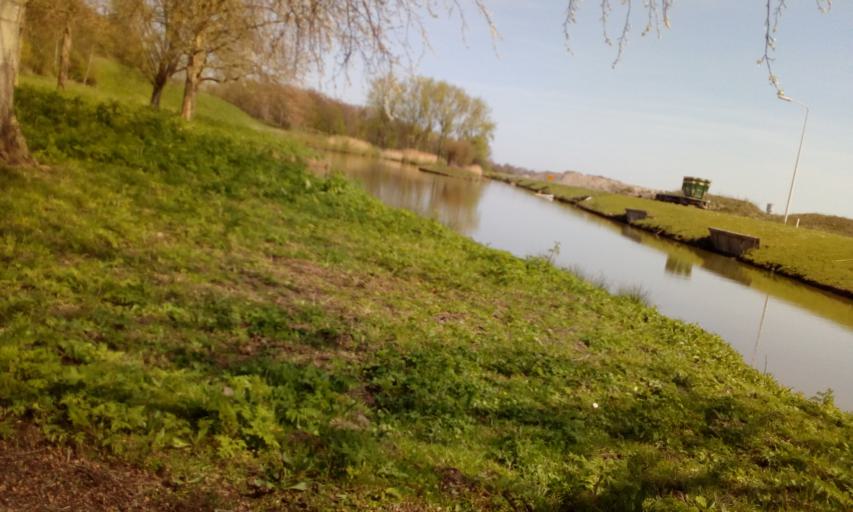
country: NL
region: South Holland
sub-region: Gemeente Rijswijk
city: Rijswijk
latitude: 52.0222
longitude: 4.3318
